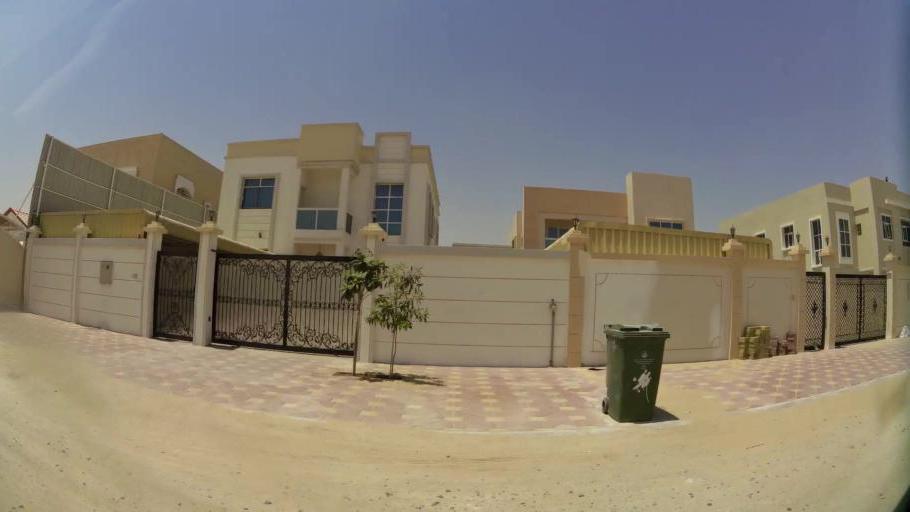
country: AE
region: Ajman
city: Ajman
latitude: 25.4020
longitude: 55.5218
